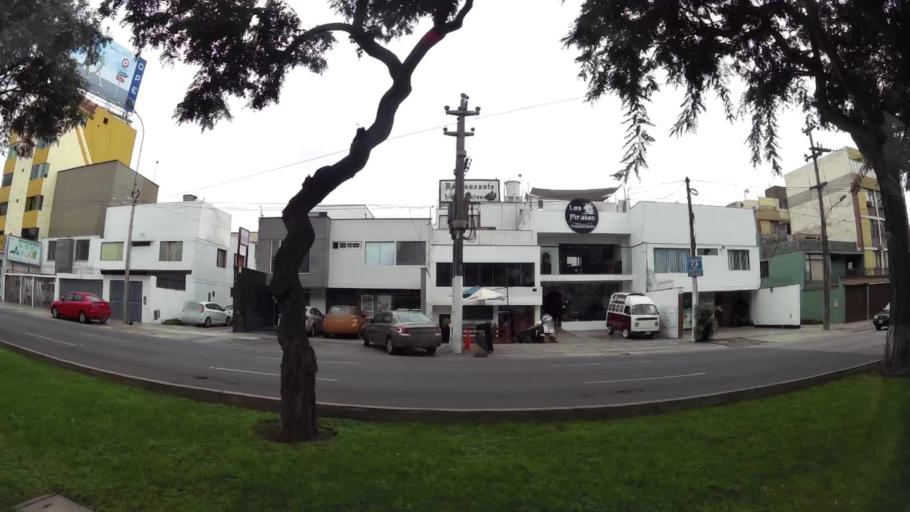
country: PE
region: Lima
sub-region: Lima
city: San Isidro
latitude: -12.1021
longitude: -77.0217
